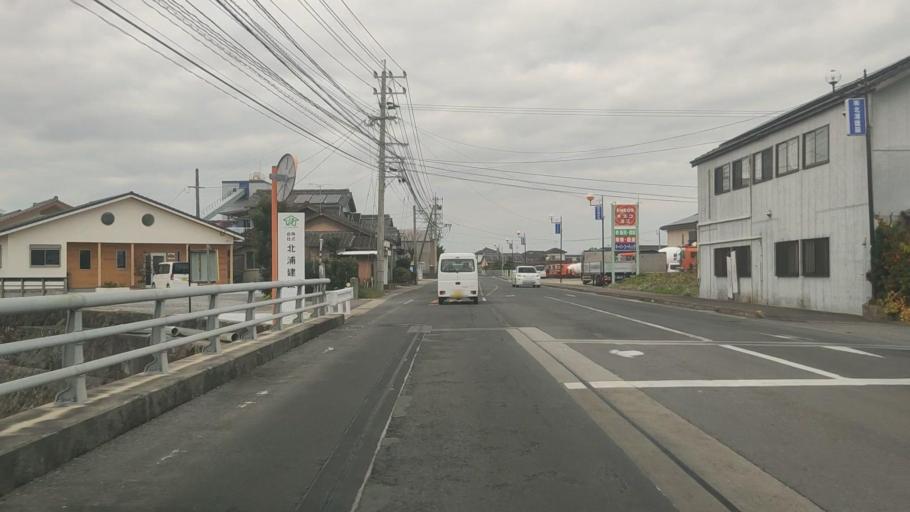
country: JP
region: Nagasaki
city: Shimabara
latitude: 32.8625
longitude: 130.3245
